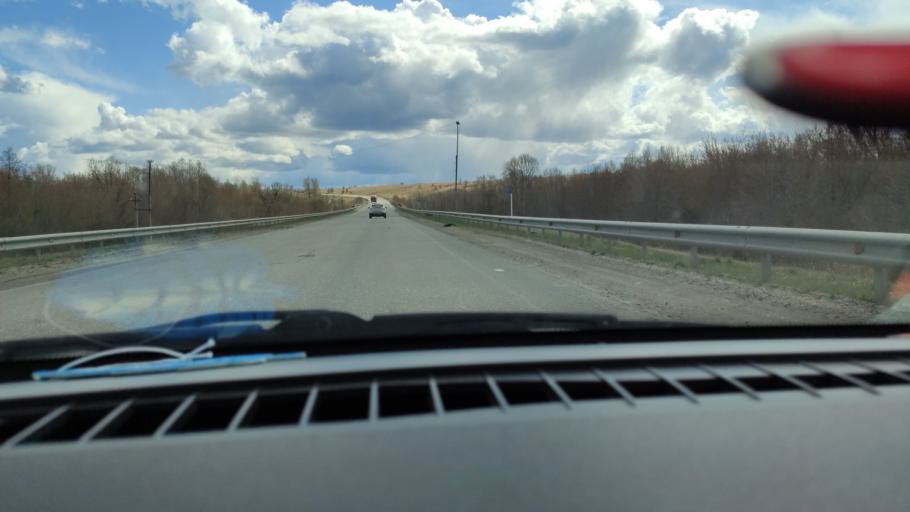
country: RU
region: Samara
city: Varlamovo
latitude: 53.1303
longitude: 48.2879
